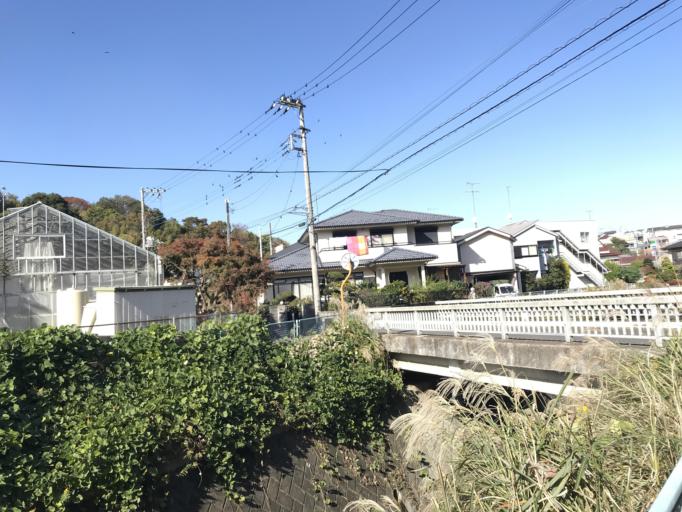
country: JP
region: Tokyo
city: Chofugaoka
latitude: 35.5988
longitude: 139.5656
